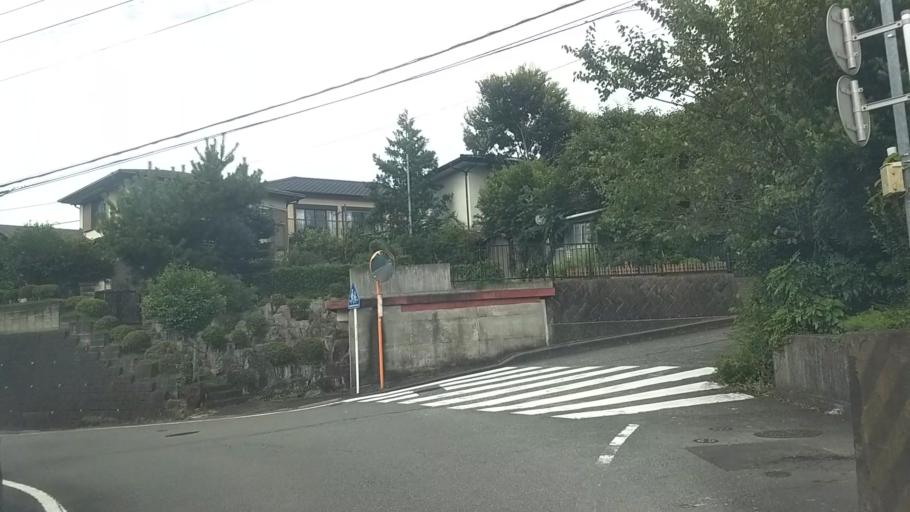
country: JP
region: Shizuoka
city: Ito
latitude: 34.9748
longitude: 138.9495
